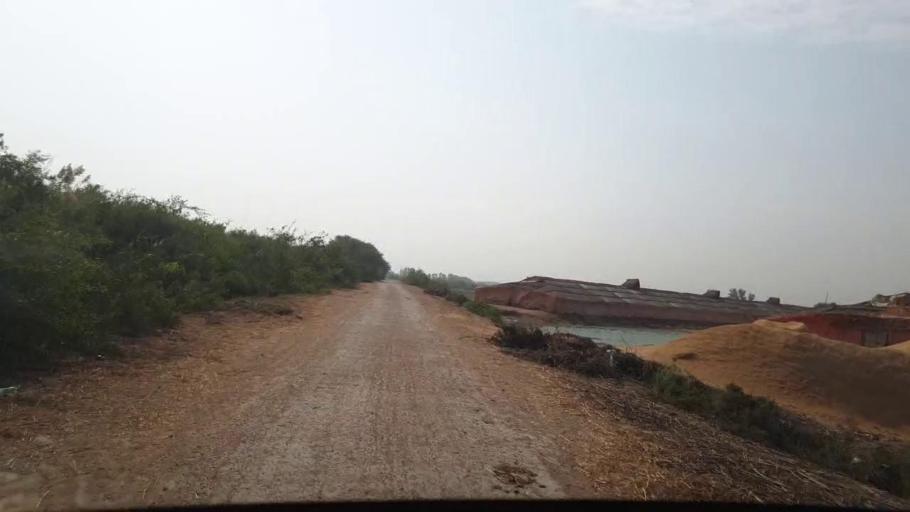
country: PK
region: Sindh
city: Chuhar Jamali
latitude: 24.3793
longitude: 67.9407
